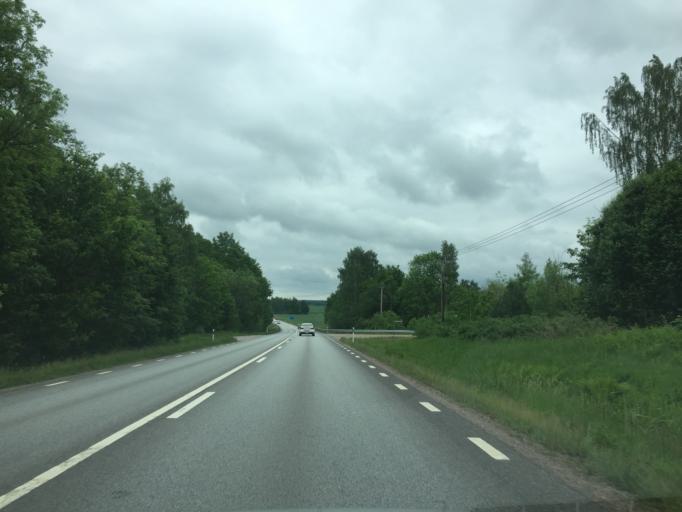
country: SE
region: OErebro
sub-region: Orebro Kommun
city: Odensbacken
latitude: 59.1545
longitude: 15.4699
